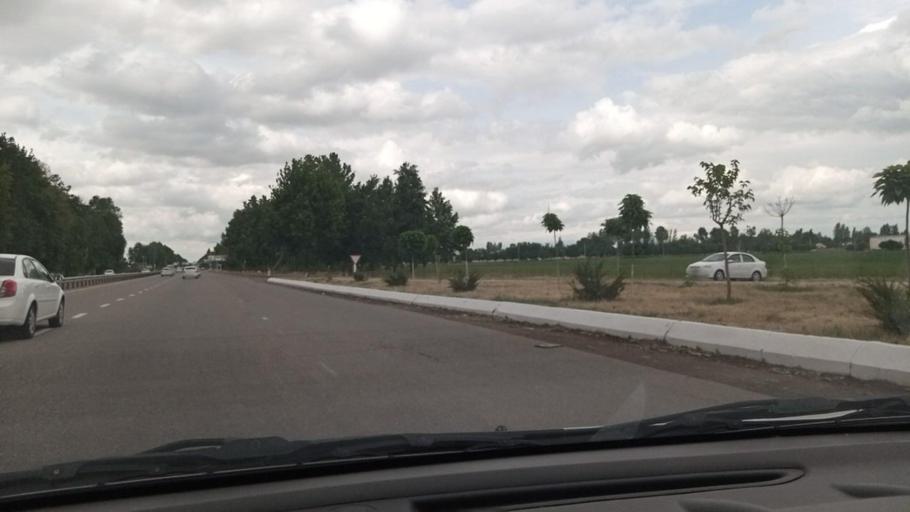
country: UZ
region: Toshkent Shahri
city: Bektemir
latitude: 41.2202
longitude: 69.4026
